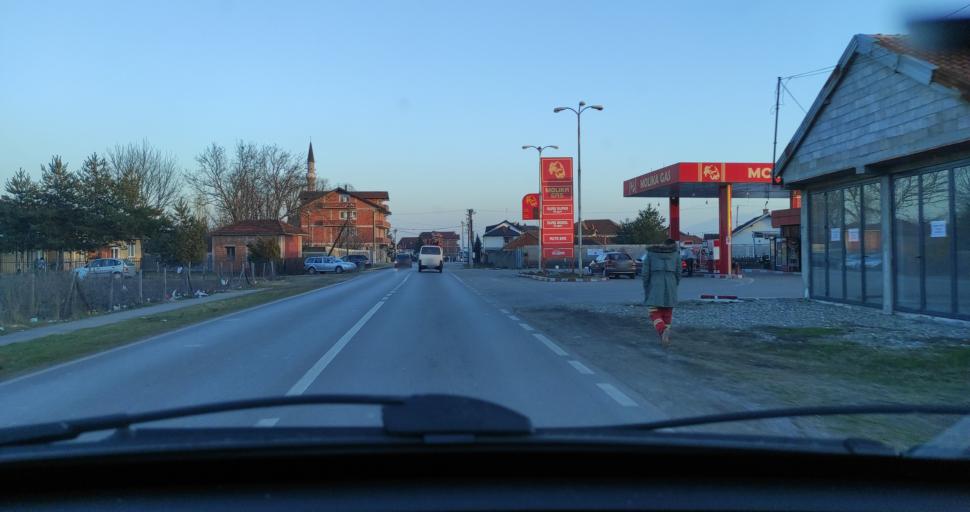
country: XK
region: Gjakova
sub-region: Komuna e Gjakoves
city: Gjakove
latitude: 42.4318
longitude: 20.3814
